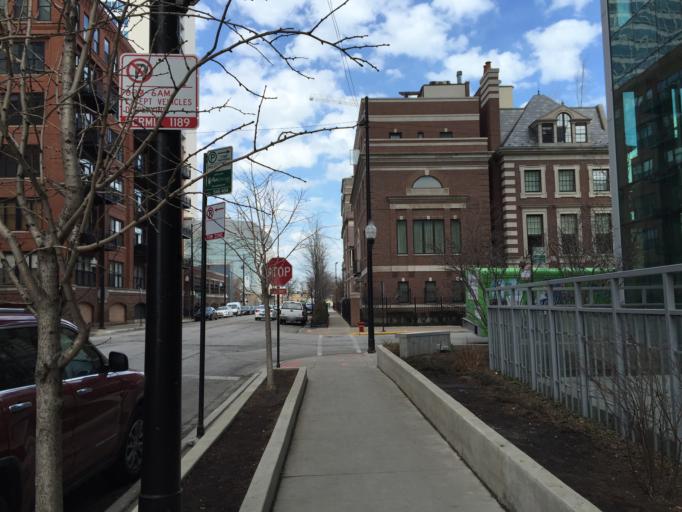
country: US
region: Illinois
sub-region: Cook County
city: Chicago
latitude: 41.8944
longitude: -87.6415
